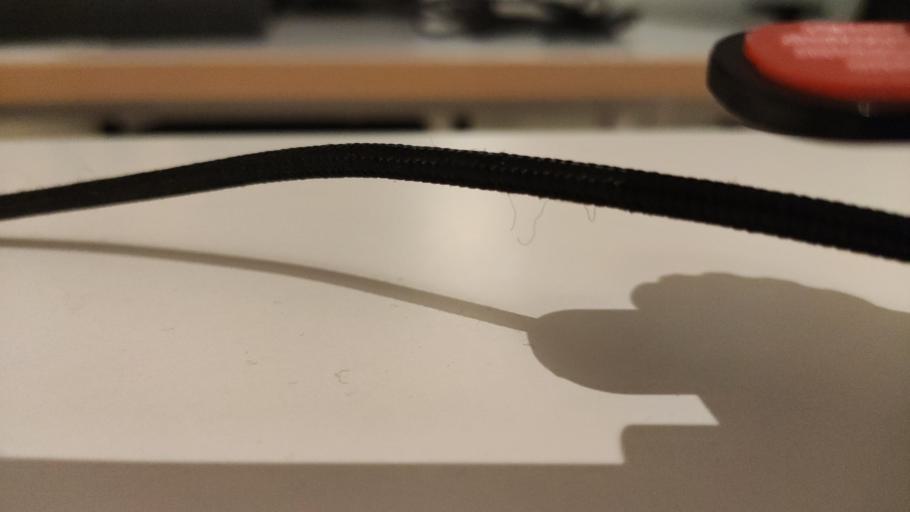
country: RU
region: Moskovskaya
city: Malaya Dubna
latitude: 55.8656
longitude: 38.9632
